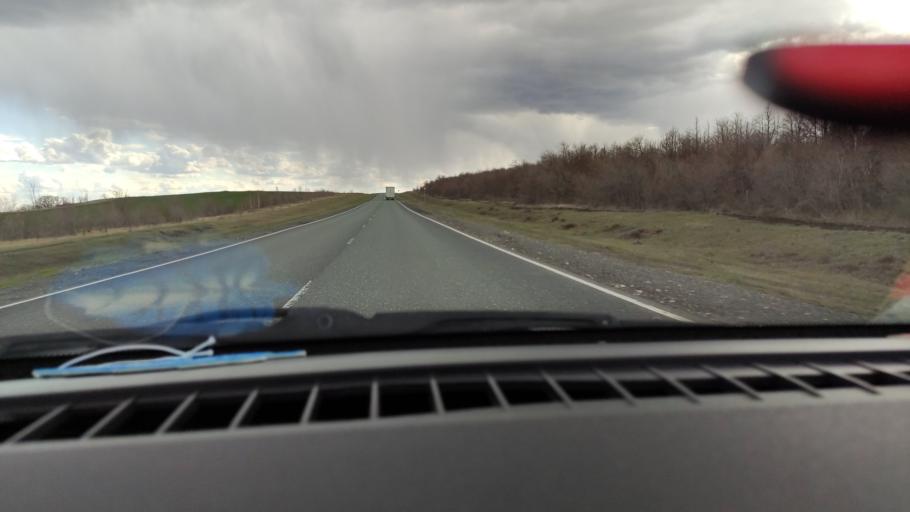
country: RU
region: Saratov
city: Balakovo
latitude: 52.1935
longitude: 47.8558
